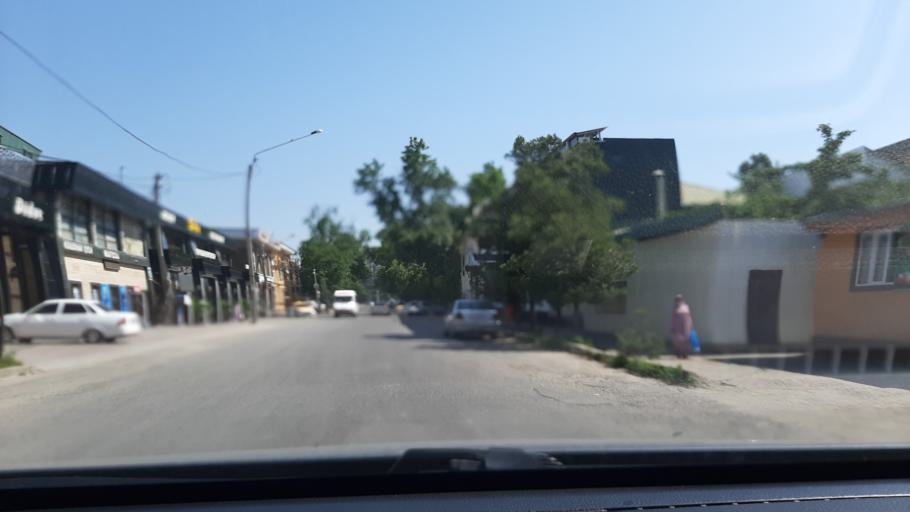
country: TJ
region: Dushanbe
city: Dushanbe
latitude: 38.5560
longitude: 68.7567
